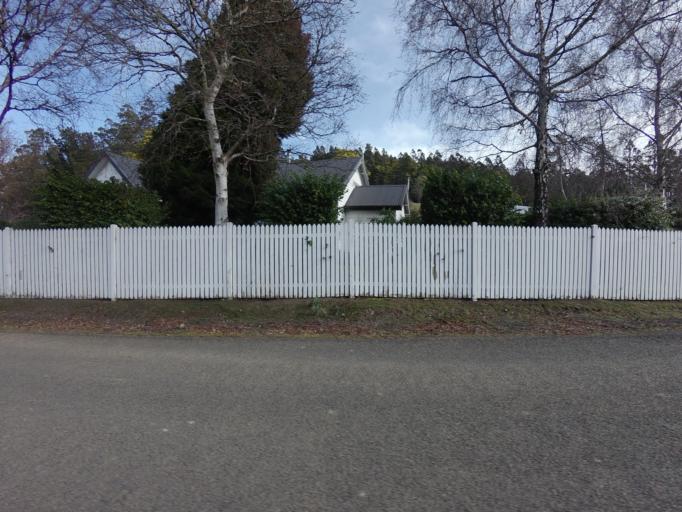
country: AU
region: Tasmania
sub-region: Kingborough
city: Margate
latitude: -43.0204
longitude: 147.1643
